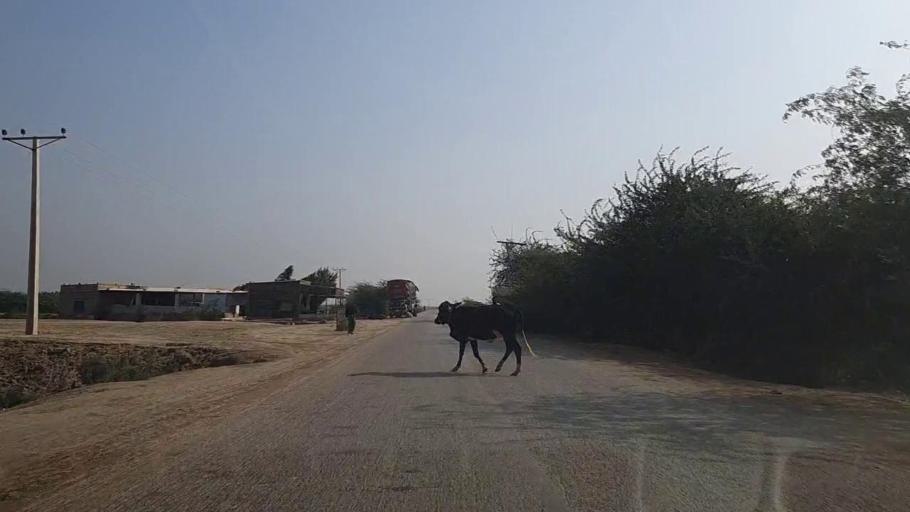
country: PK
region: Sindh
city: Keti Bandar
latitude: 24.2307
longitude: 67.6094
